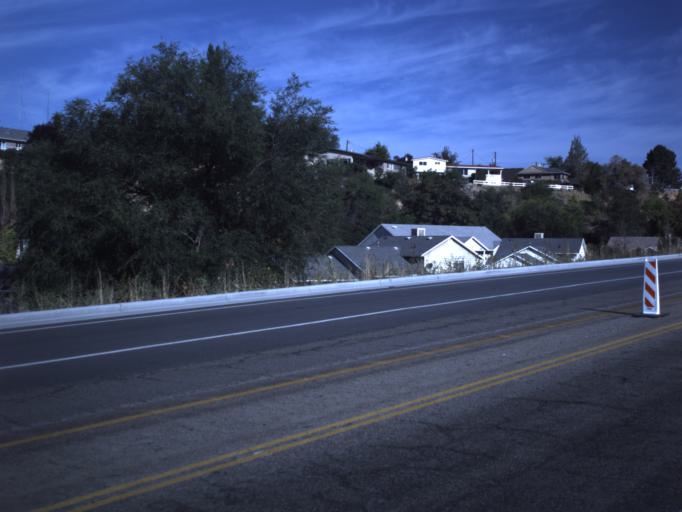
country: US
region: Utah
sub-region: Utah County
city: Orem
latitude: 40.2689
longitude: -111.6724
